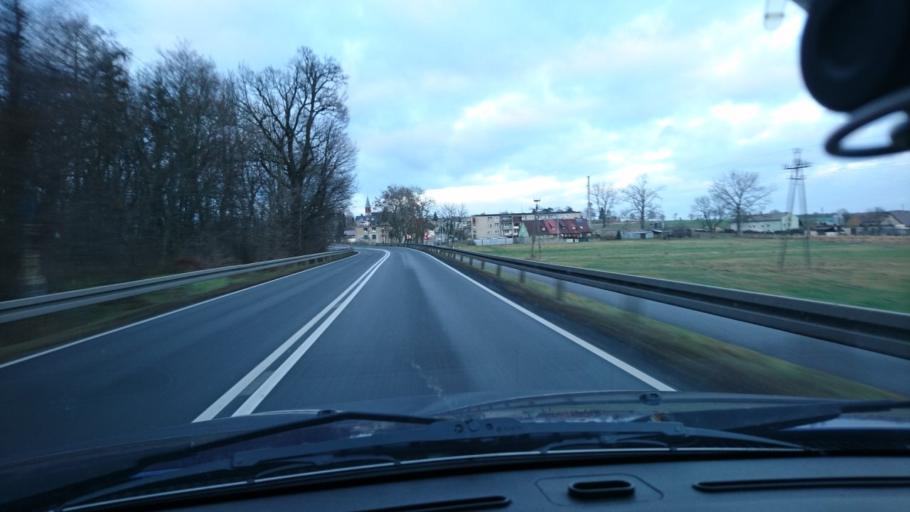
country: PL
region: Greater Poland Voivodeship
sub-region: Powiat ostrzeszowski
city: Ostrzeszow
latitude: 51.3827
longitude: 17.9485
